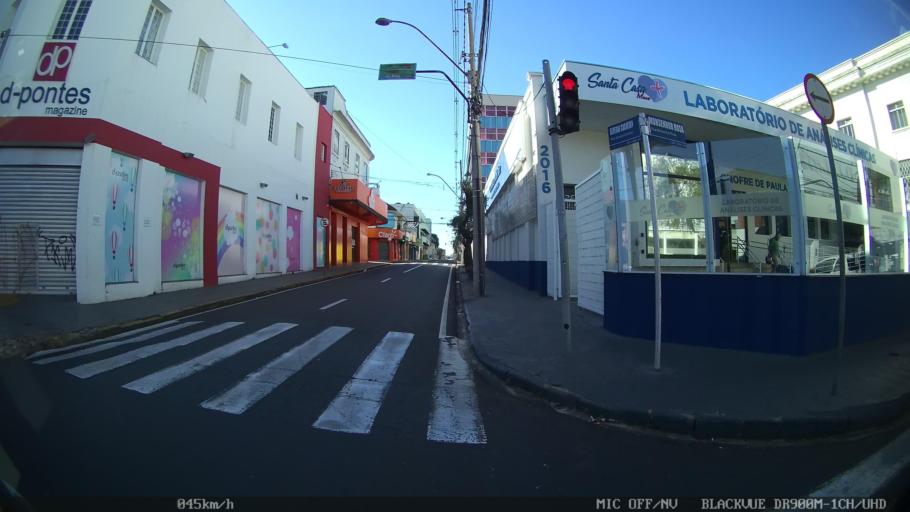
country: BR
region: Sao Paulo
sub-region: Franca
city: Franca
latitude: -20.5359
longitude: -47.4008
